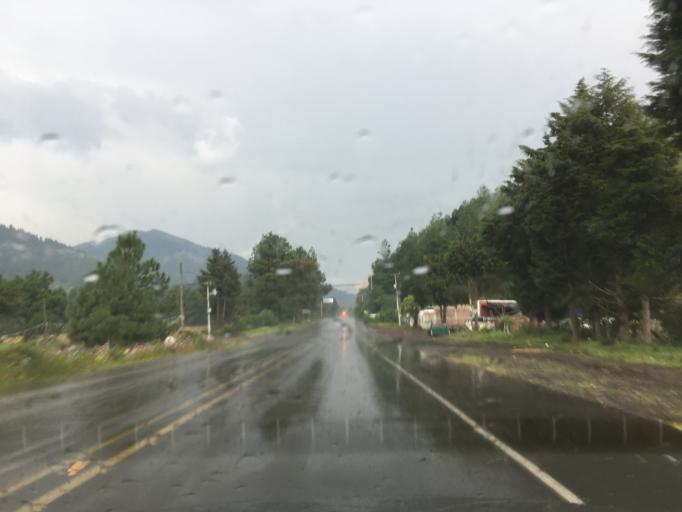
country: MX
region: Michoacan
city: Angahuan
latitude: 19.5639
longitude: -102.2357
